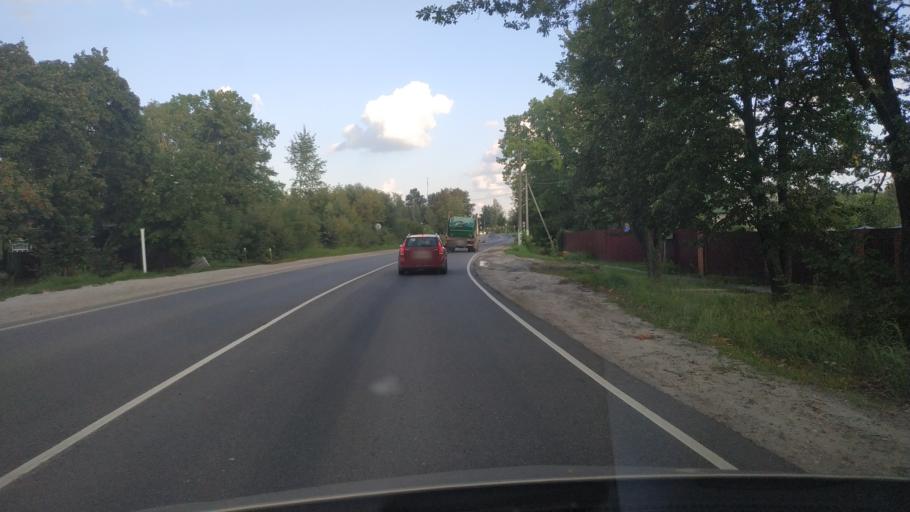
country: RU
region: Moskovskaya
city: Shatura
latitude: 55.5789
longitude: 39.4840
